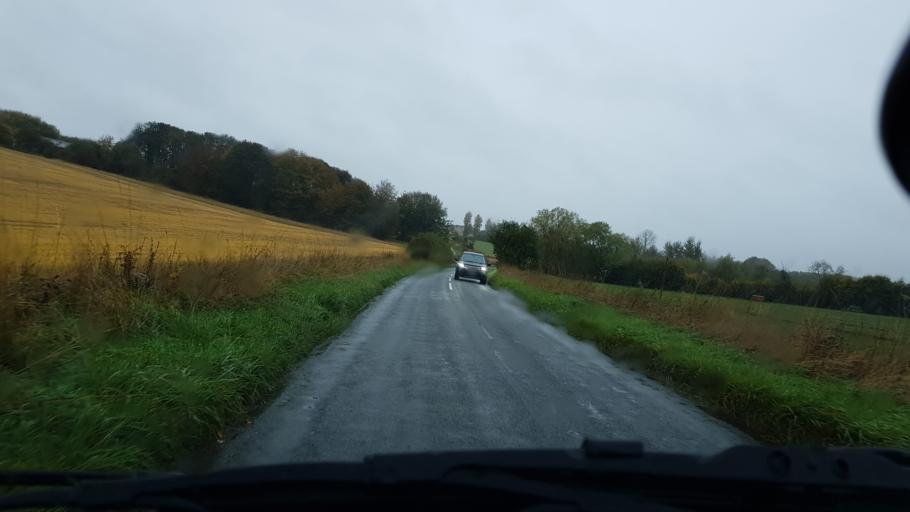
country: GB
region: England
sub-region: Oxfordshire
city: Burford
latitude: 51.8003
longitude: -1.6206
